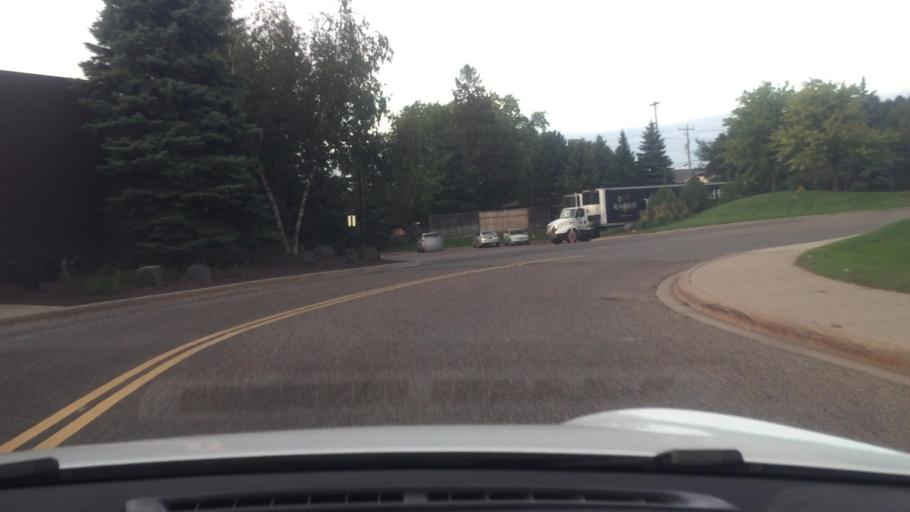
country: US
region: Minnesota
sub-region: Ramsey County
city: Shoreview
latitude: 45.0810
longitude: -93.1190
